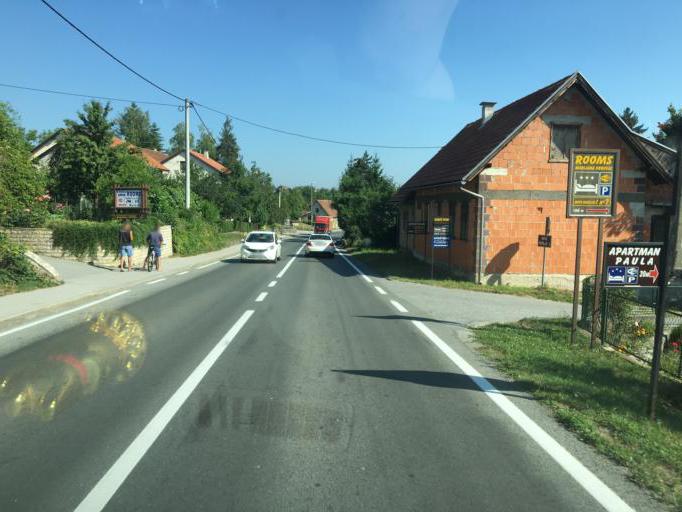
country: HR
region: Karlovacka
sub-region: Grad Karlovac
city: Slunj
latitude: 45.1107
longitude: 15.5853
